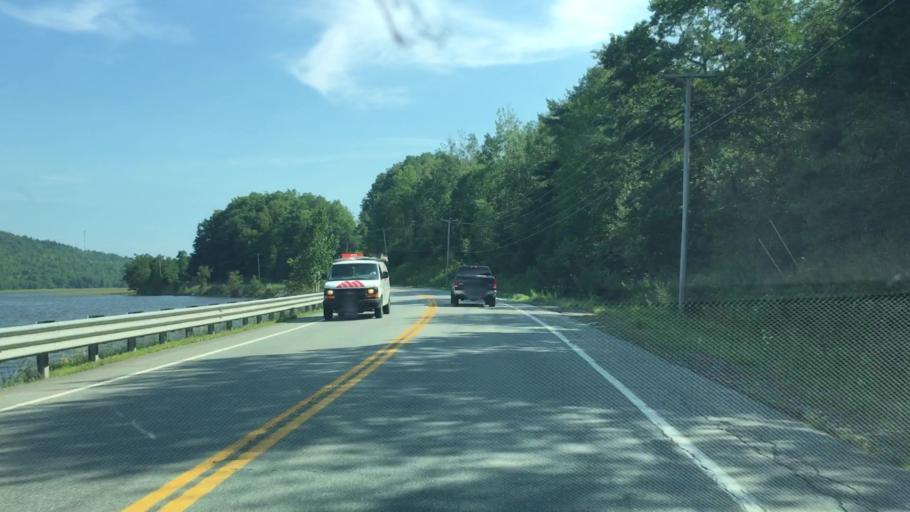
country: US
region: Maine
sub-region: Waldo County
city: Frankfort
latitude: 44.6006
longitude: -68.8678
